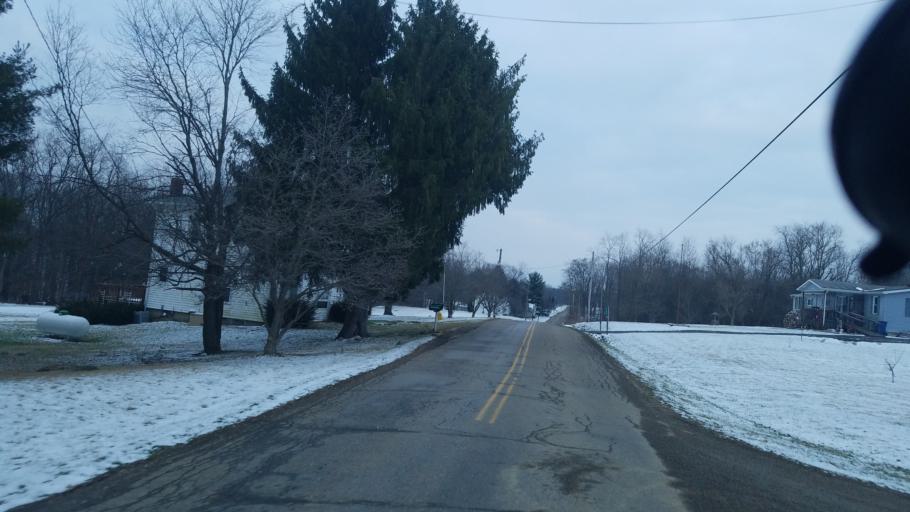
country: US
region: Ohio
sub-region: Knox County
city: Fredericktown
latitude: 40.4241
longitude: -82.5824
